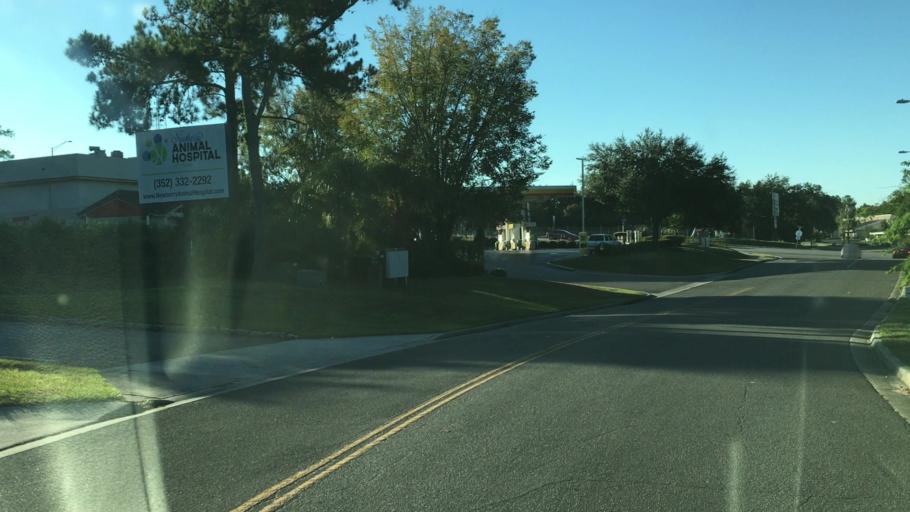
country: US
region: Florida
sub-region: Alachua County
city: Alachua
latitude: 29.6901
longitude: -82.4504
